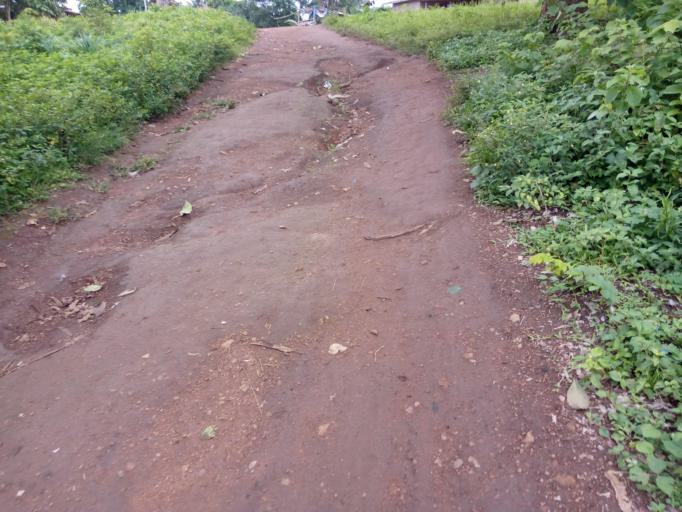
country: SL
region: Eastern Province
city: Buedu
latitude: 8.4555
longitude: -10.3329
